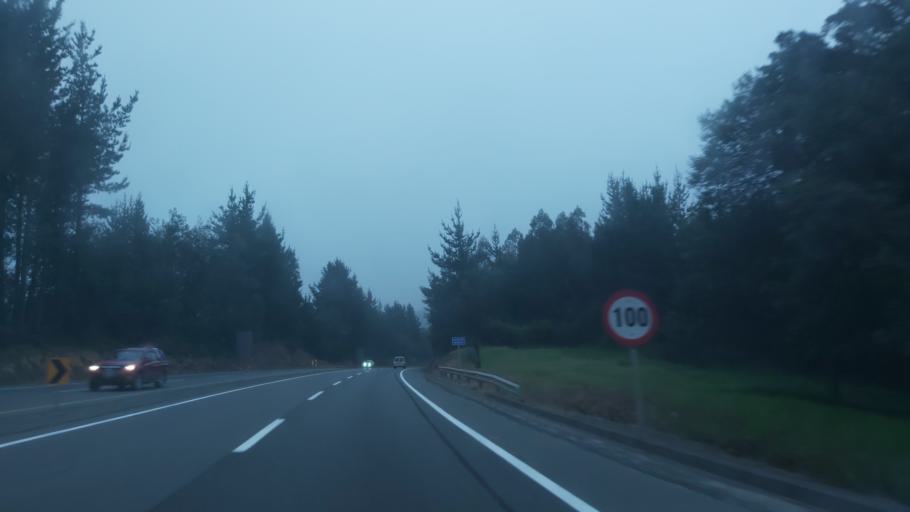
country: CL
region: Biobio
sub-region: Provincia de Concepcion
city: Penco
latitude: -36.7381
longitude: -72.8936
